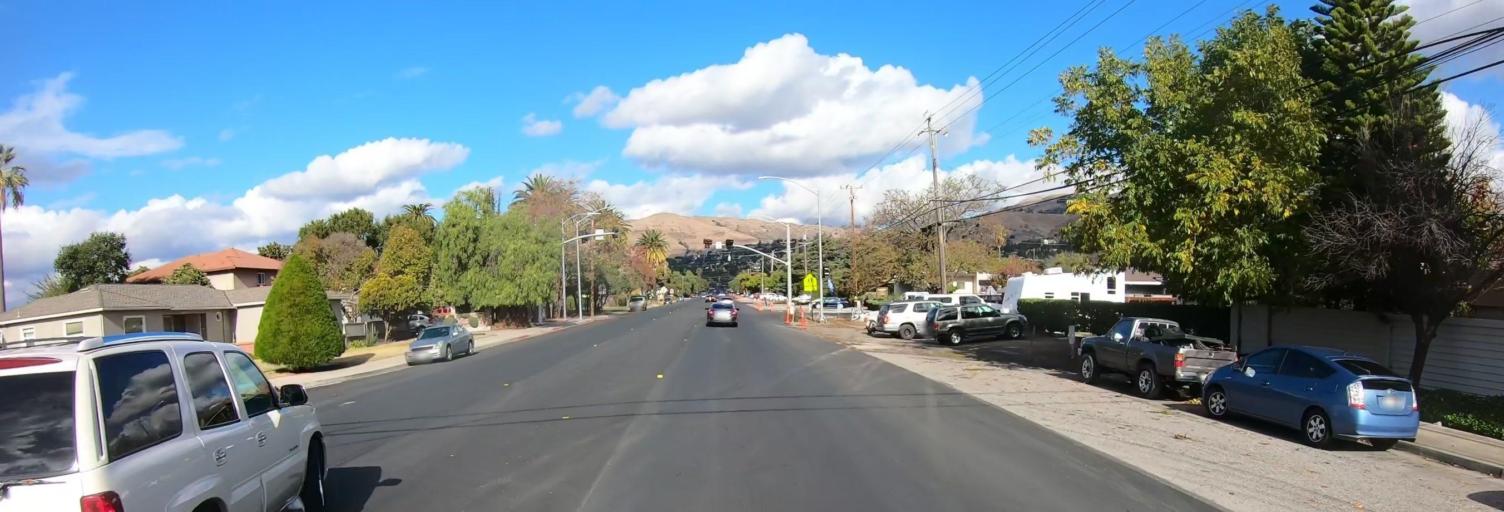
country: US
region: California
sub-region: Santa Clara County
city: Alum Rock
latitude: 37.3691
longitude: -121.8253
